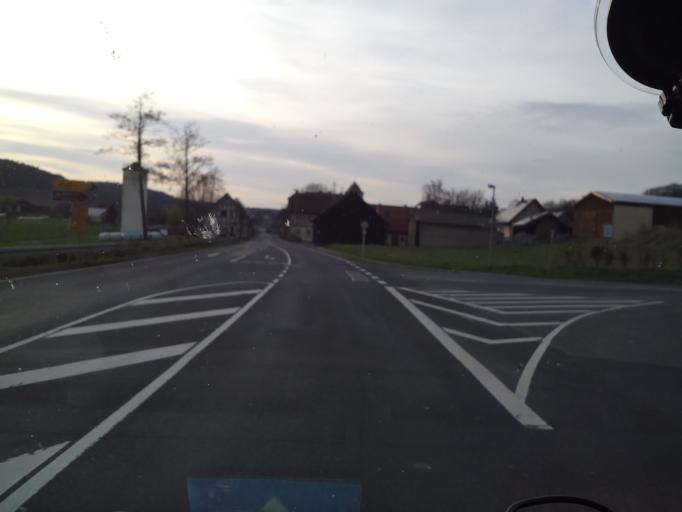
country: DE
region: Bavaria
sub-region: Regierungsbezirk Unterfranken
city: Pfarrweisach
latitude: 50.1589
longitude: 10.7325
